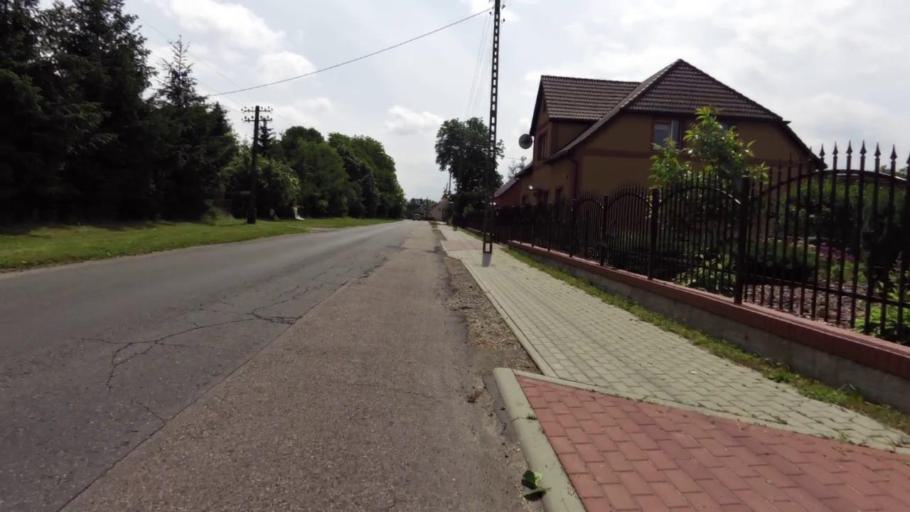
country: PL
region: West Pomeranian Voivodeship
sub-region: Powiat goleniowski
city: Stepnica
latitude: 53.7313
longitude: 14.6624
